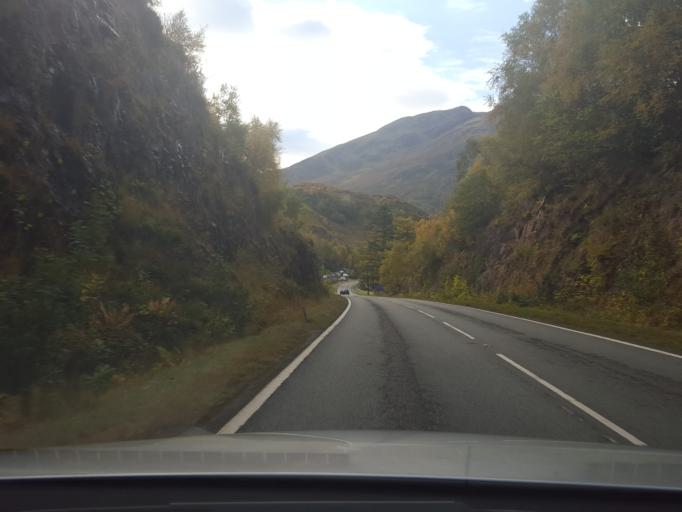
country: GB
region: Scotland
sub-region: Highland
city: Fort William
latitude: 57.2218
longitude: -5.4158
